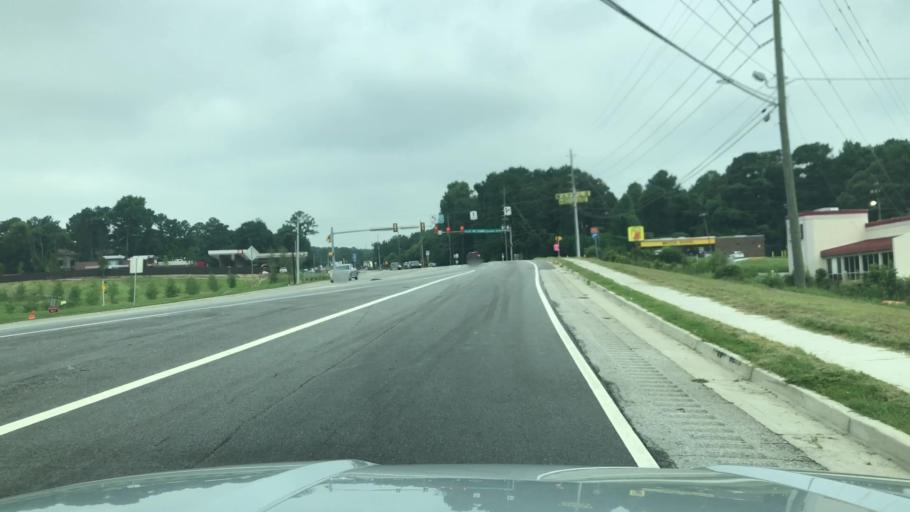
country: US
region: Georgia
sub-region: Cobb County
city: Mableton
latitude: 33.7750
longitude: -84.5608
